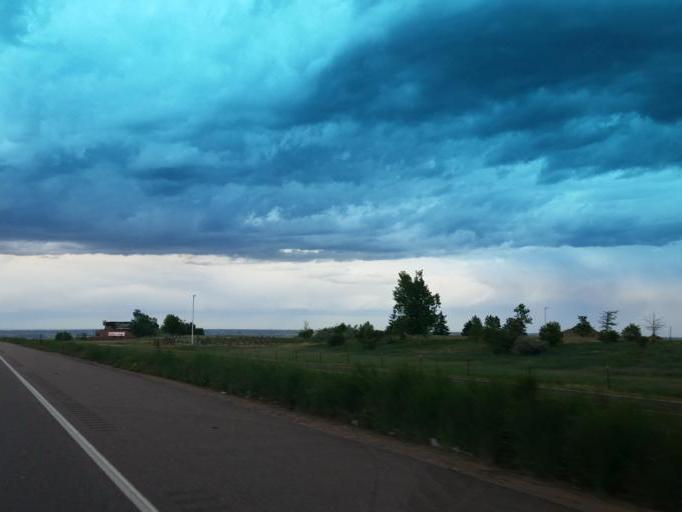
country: US
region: Colorado
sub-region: Weld County
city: Windsor
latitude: 40.4463
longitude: -104.9920
